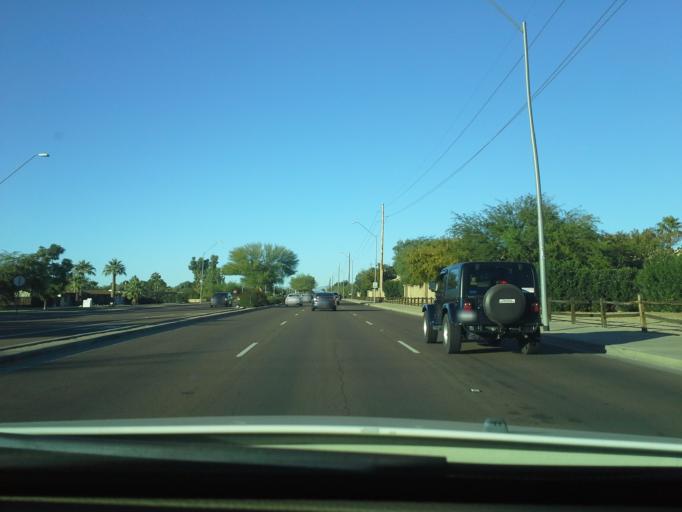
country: US
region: Arizona
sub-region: Maricopa County
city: Paradise Valley
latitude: 33.5896
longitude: -111.9259
